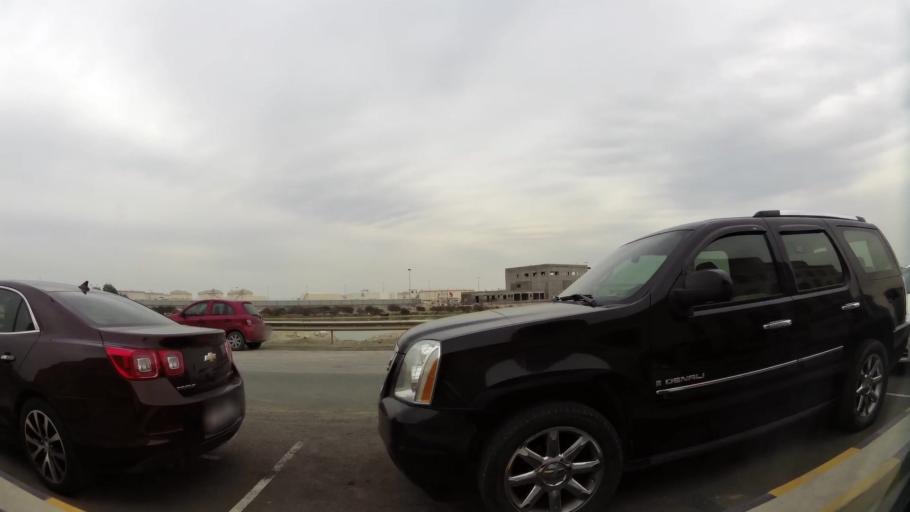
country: BH
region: Northern
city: Sitrah
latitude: 26.1432
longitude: 50.6154
